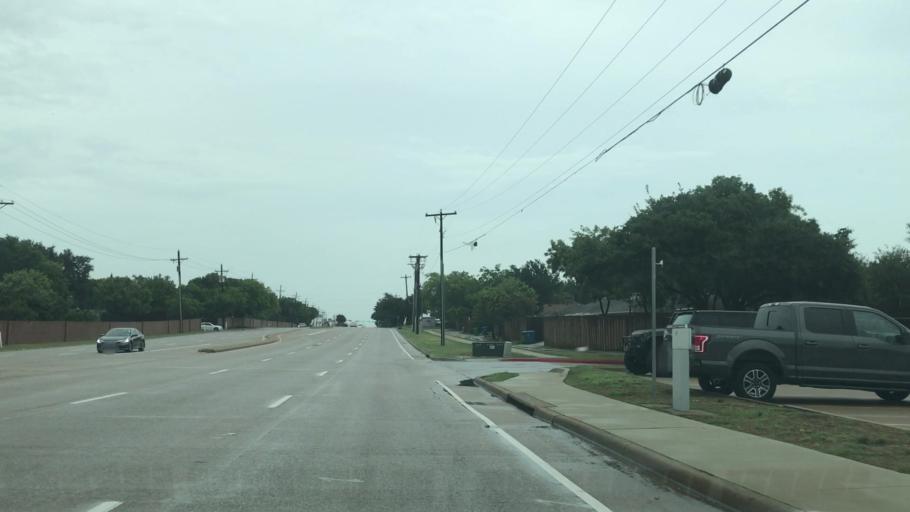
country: US
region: Texas
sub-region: Denton County
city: Lewisville
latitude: 33.0423
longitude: -97.0417
